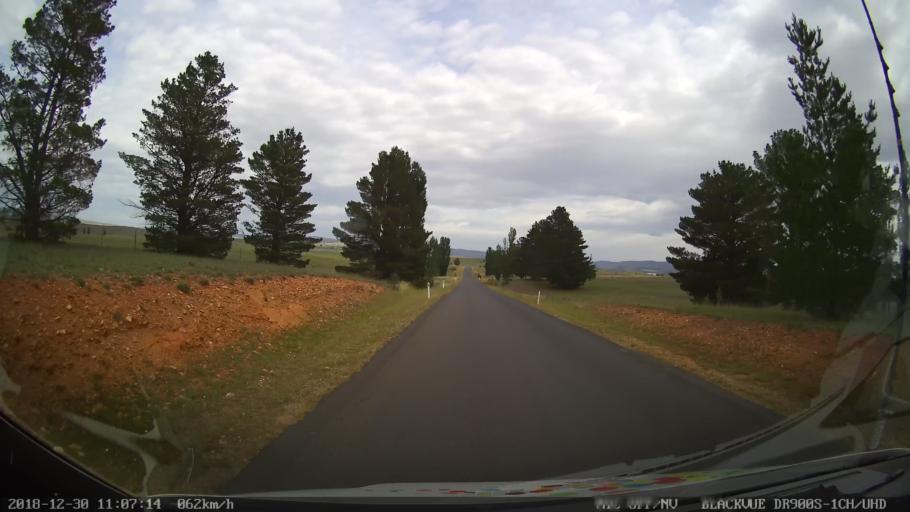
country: AU
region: New South Wales
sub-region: Snowy River
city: Berridale
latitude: -36.5023
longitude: 148.8227
